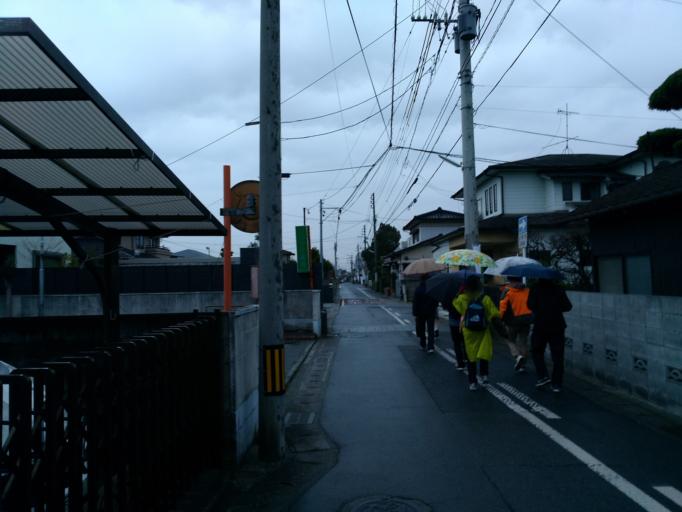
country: JP
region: Saga Prefecture
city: Saga-shi
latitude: 33.2481
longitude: 130.3072
